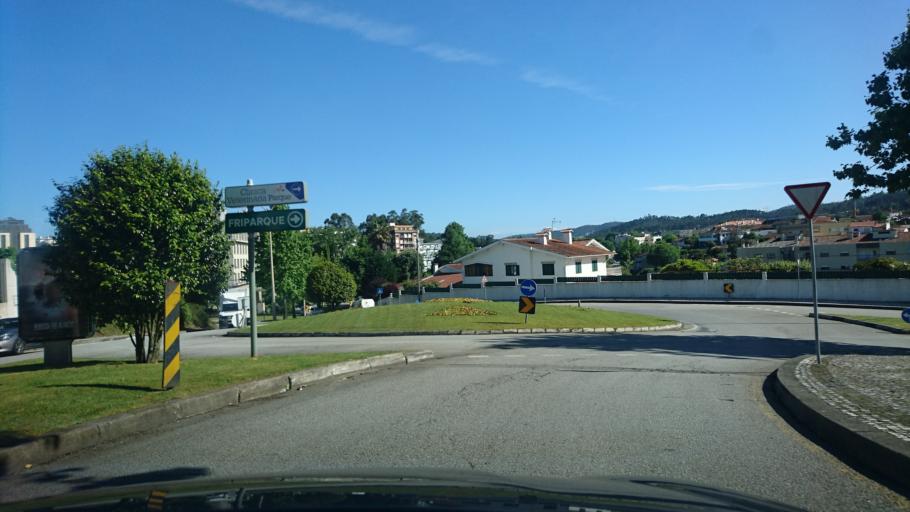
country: PT
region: Aveiro
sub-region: Sao Joao da Madeira
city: Sao Joao da Madeira
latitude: 40.8932
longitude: -8.4849
